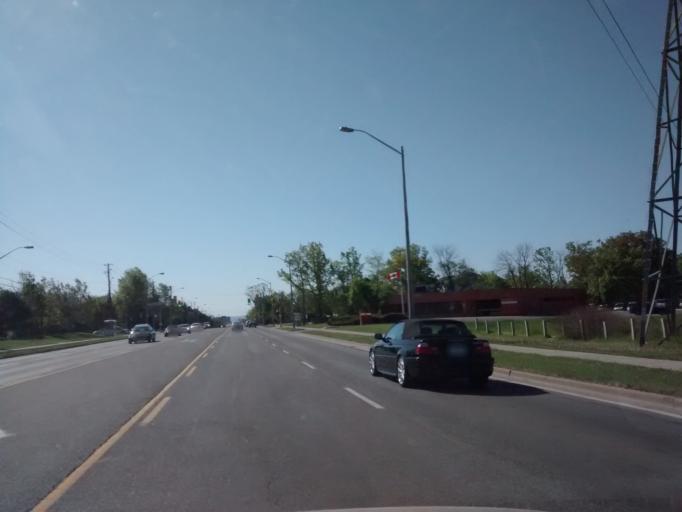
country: CA
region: Ontario
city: Burlington
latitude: 43.3622
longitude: -79.8181
